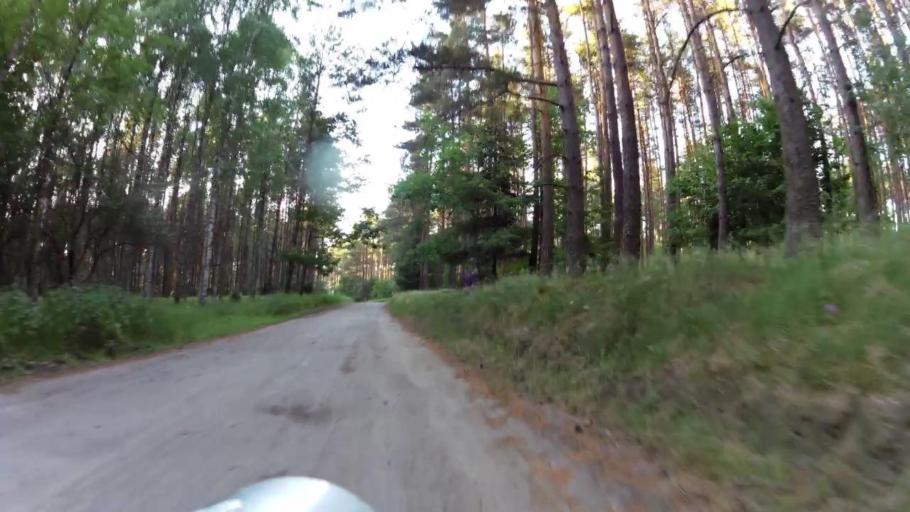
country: PL
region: West Pomeranian Voivodeship
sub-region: Powiat szczecinecki
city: Szczecinek
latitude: 53.8235
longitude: 16.6924
